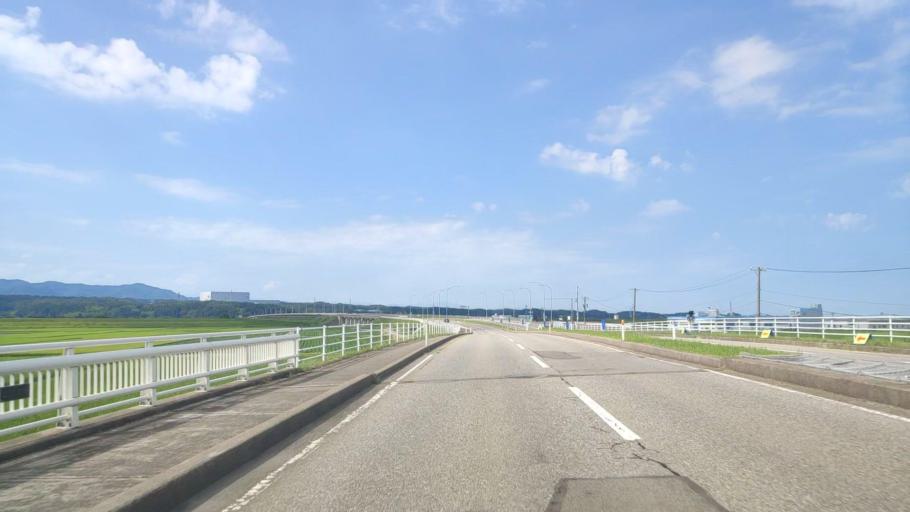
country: JP
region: Ishikawa
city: Matsuto
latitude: 36.4667
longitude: 136.5788
